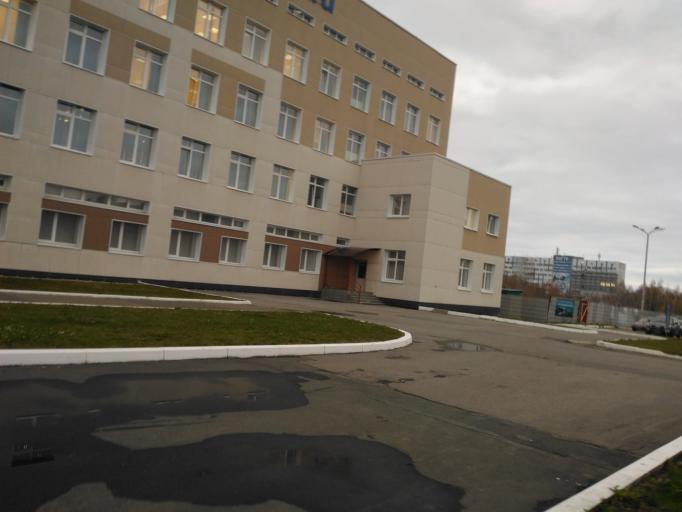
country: RU
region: Ulyanovsk
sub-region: Ulyanovskiy Rayon
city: Ulyanovsk
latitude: 54.3485
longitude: 48.3860
